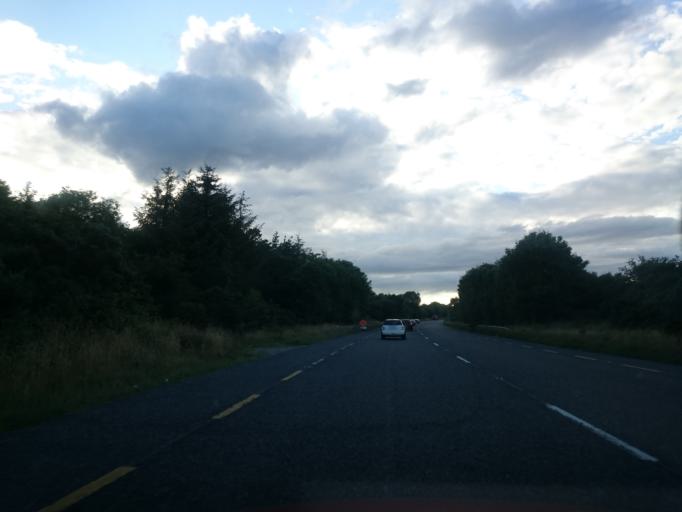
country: IE
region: Leinster
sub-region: Loch Garman
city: Loch Garman
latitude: 52.3056
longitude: -6.4767
